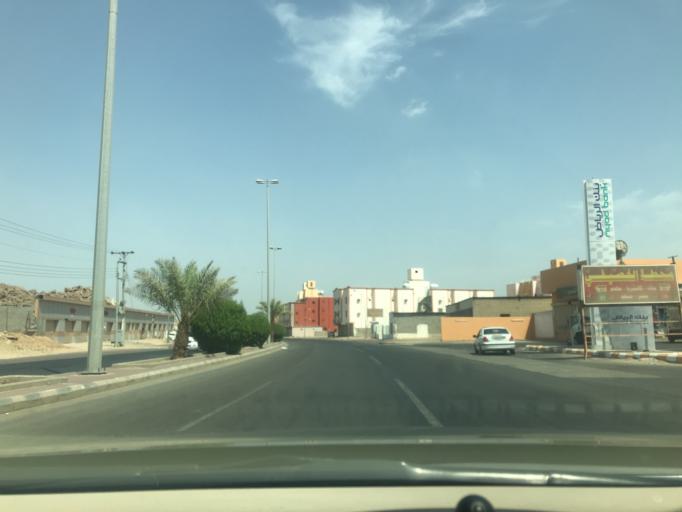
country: SA
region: Makkah
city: Al Jumum
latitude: 21.6253
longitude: 39.6692
